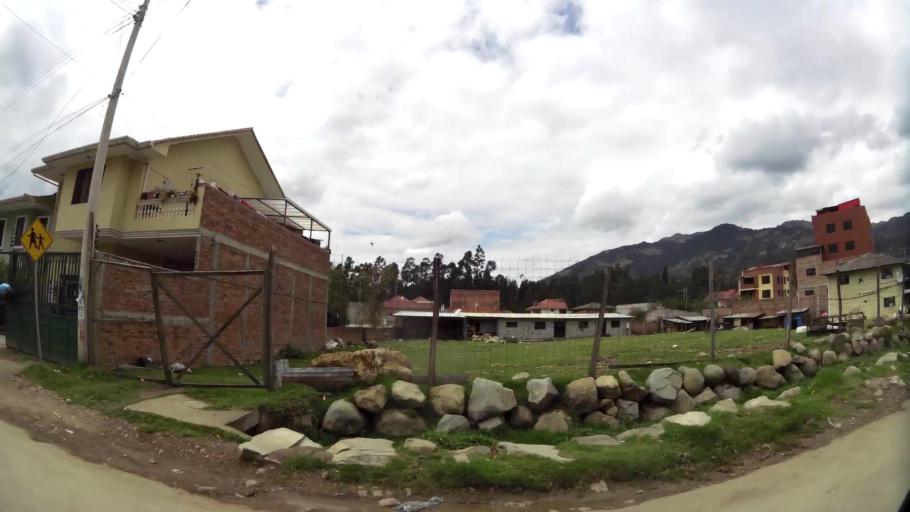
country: EC
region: Azuay
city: Cuenca
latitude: -2.8799
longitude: -79.0617
